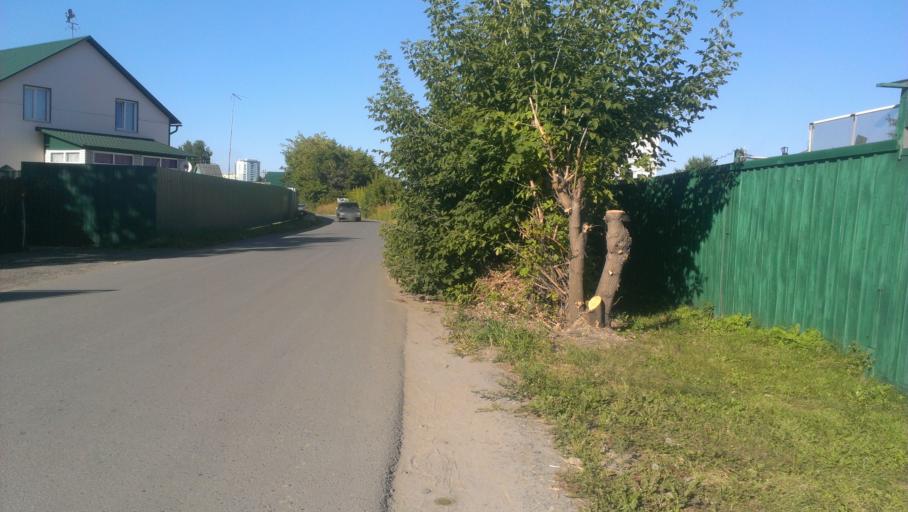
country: RU
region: Altai Krai
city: Novosilikatnyy
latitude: 53.3212
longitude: 83.6798
